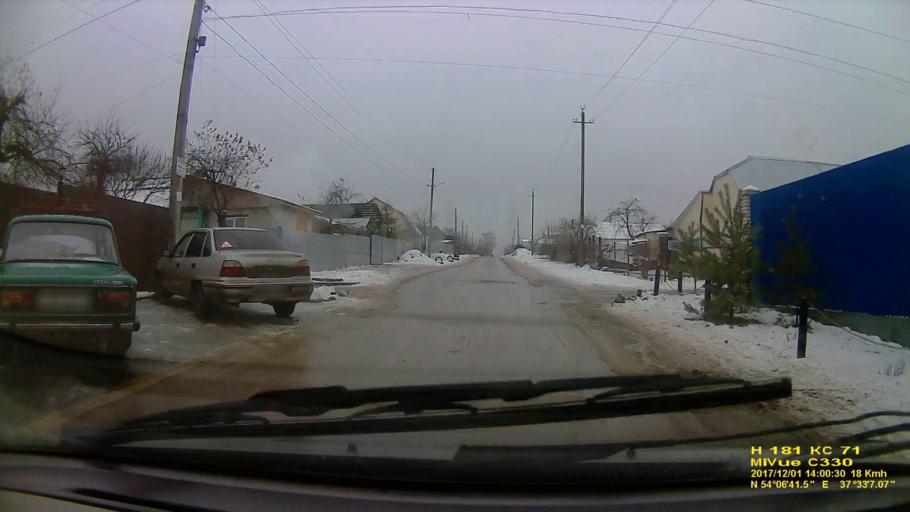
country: RU
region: Tula
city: Kosaya Gora
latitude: 54.1116
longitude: 37.5519
